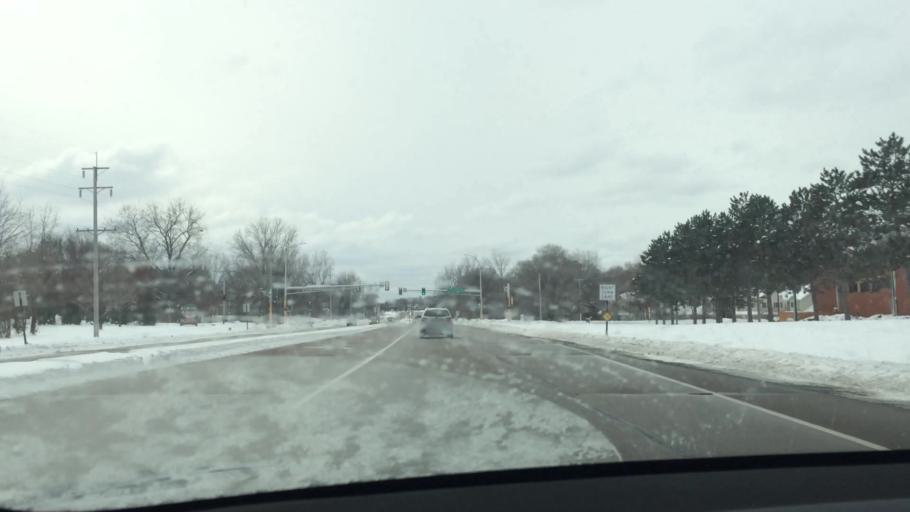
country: US
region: Minnesota
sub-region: Anoka County
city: Circle Pines
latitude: 45.1461
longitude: -93.1548
